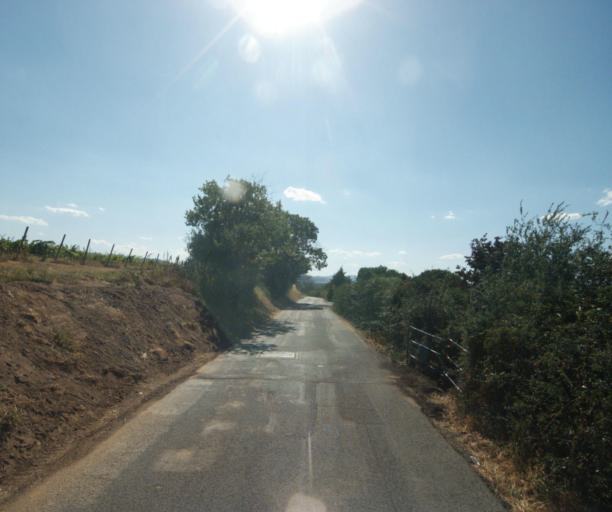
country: FR
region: Rhone-Alpes
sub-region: Departement du Rhone
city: La Tour-de-Salvagny
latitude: 45.8266
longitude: 4.7331
